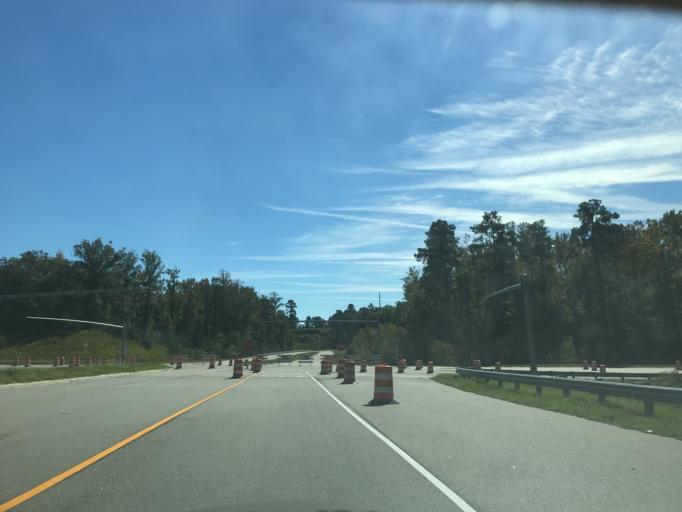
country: US
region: North Carolina
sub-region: Wake County
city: Morrisville
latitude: 35.8479
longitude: -78.8810
